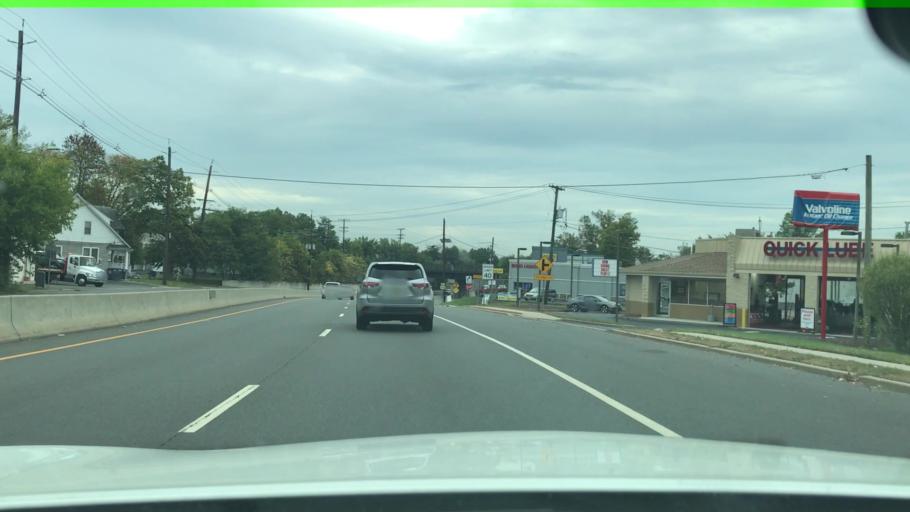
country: US
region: New Jersey
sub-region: Somerset County
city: Raritan
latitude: 40.5727
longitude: -74.6276
